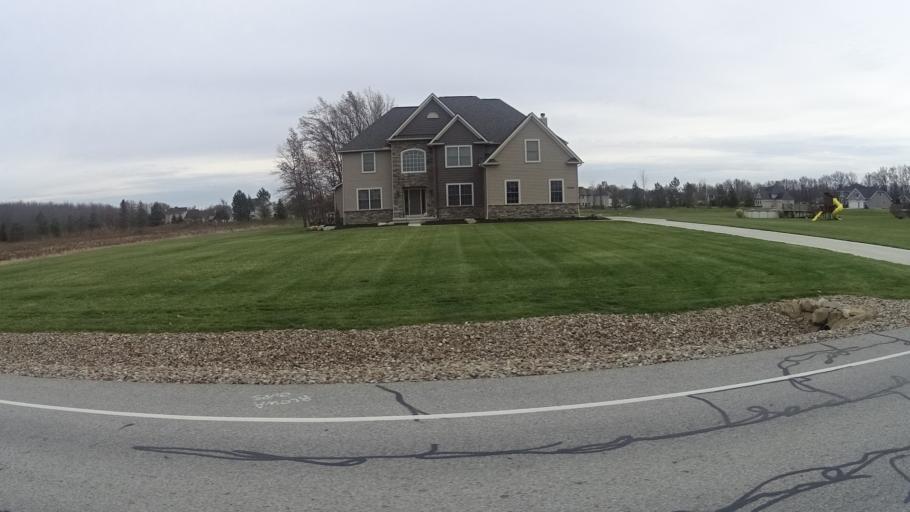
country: US
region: Ohio
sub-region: Cuyahoga County
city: Olmsted Falls
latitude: 41.3464
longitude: -81.9427
